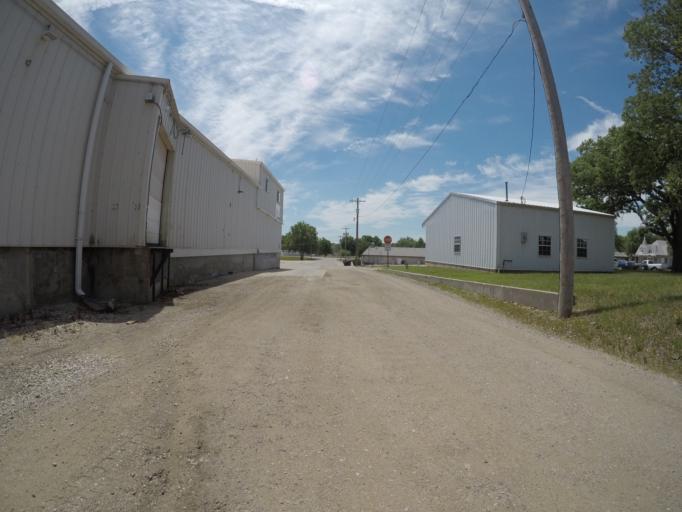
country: US
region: Kansas
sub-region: Wabaunsee County
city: Alma
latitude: 39.0115
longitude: -96.2889
